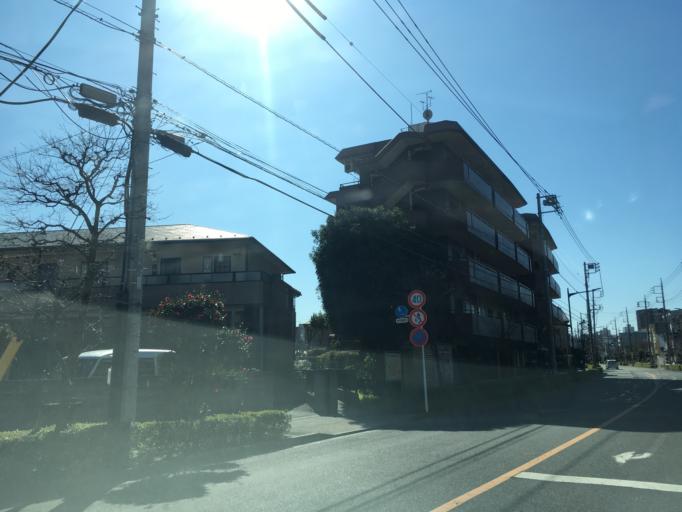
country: JP
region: Tokyo
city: Chofugaoka
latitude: 35.6527
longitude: 139.5692
